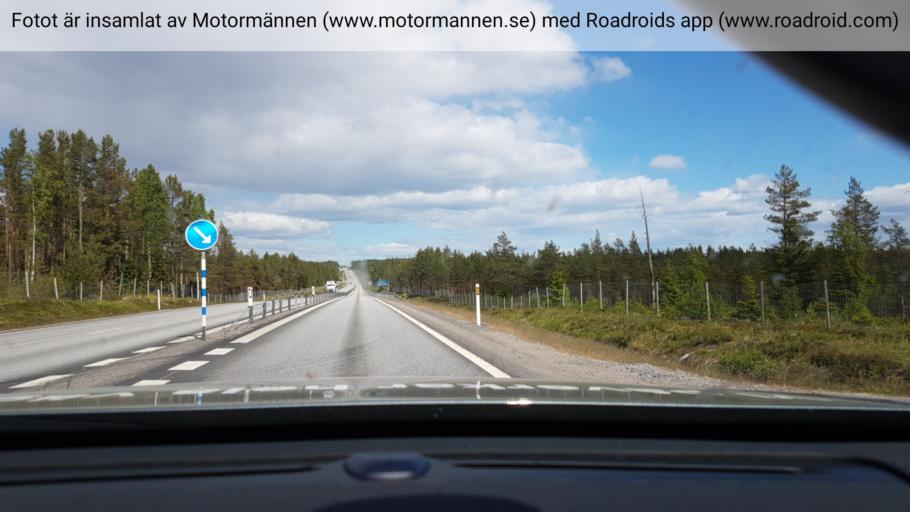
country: SE
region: Vaesterbotten
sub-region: Umea Kommun
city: Hoernefors
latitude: 63.6956
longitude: 20.0273
